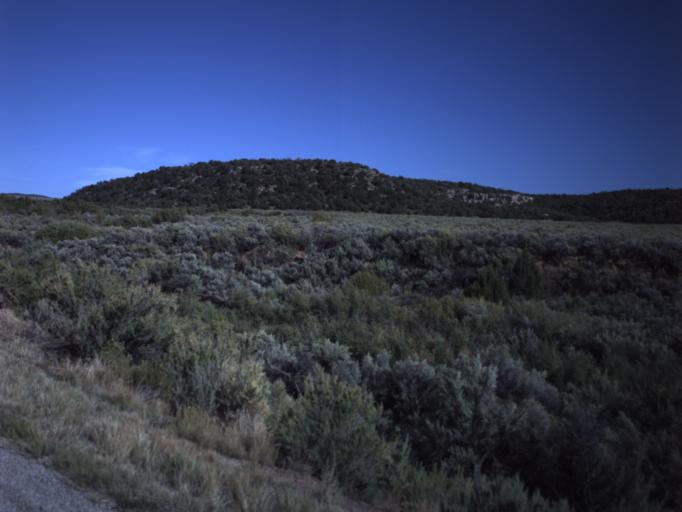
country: US
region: Utah
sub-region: Grand County
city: Moab
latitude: 38.3175
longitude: -109.3470
